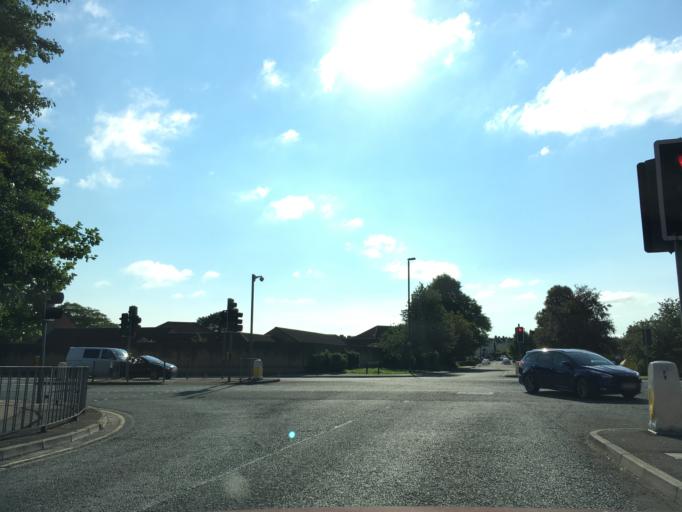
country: GB
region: England
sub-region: Somerset
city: Wells
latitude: 51.2070
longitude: -2.6550
